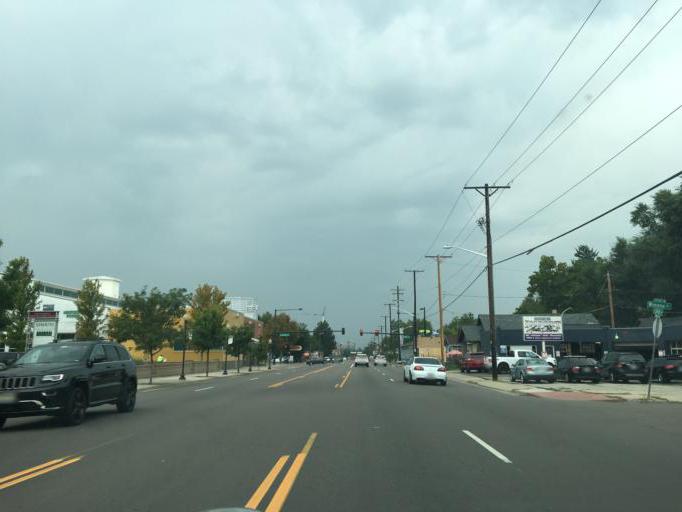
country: US
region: Colorado
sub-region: Jefferson County
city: Edgewater
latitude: 39.7694
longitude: -105.0472
